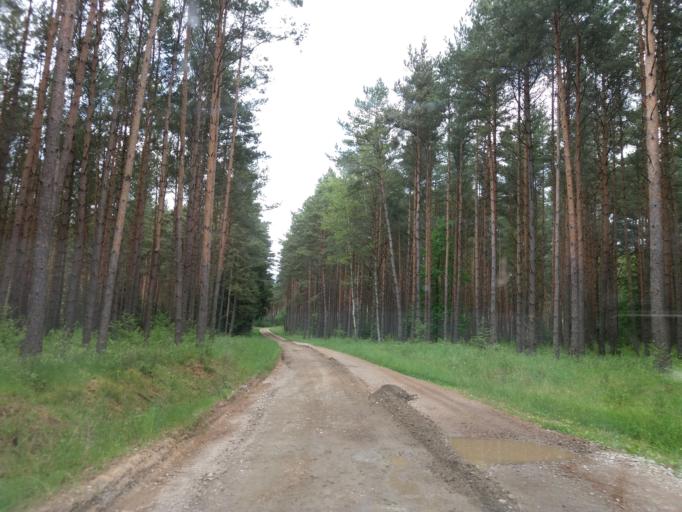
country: PL
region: West Pomeranian Voivodeship
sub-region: Powiat choszczenski
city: Drawno
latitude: 53.1967
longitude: 15.7190
